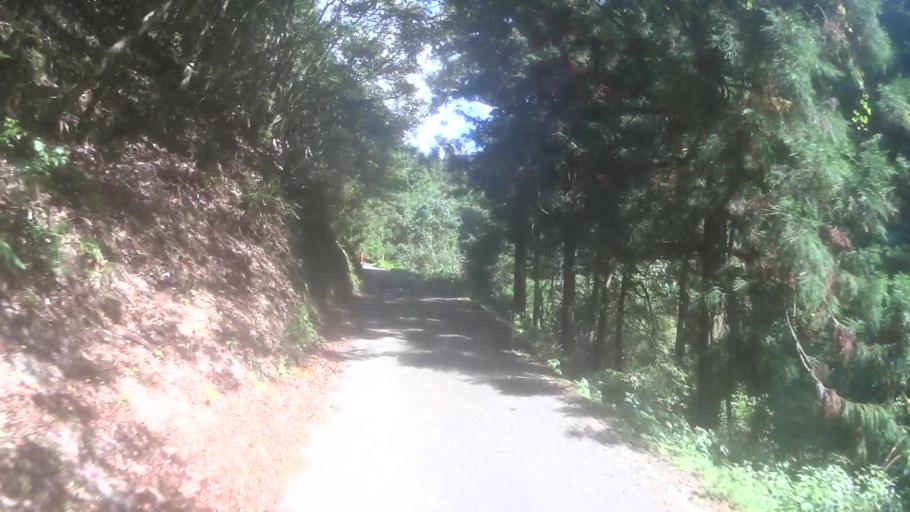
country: JP
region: Kyoto
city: Miyazu
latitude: 35.6621
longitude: 135.1267
